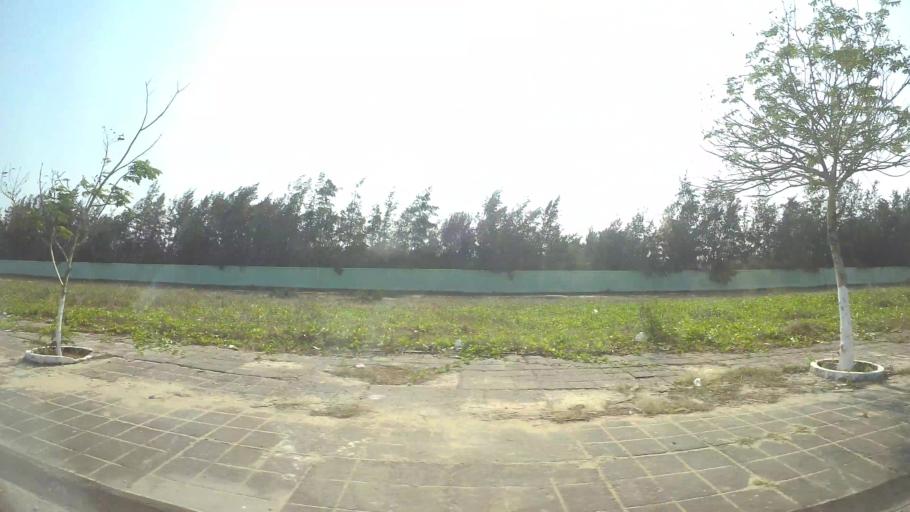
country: VN
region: Da Nang
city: Ngu Hanh Son
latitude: 15.9615
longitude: 108.2887
